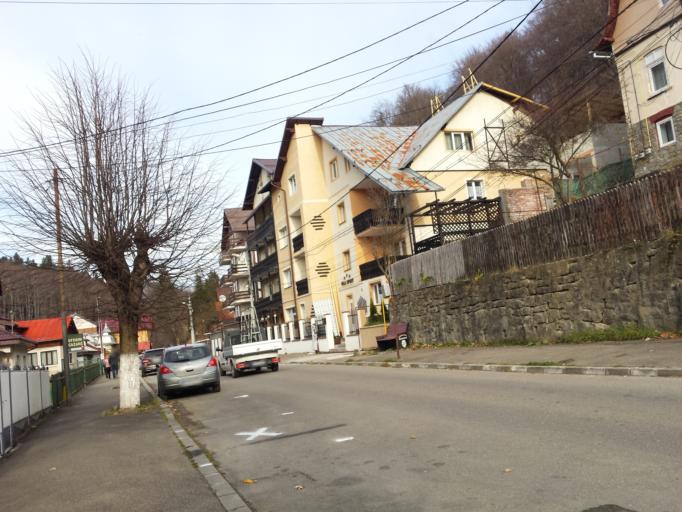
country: RO
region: Prahova
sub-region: Oras Busteni
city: Busteni
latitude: 45.4233
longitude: 25.5402
